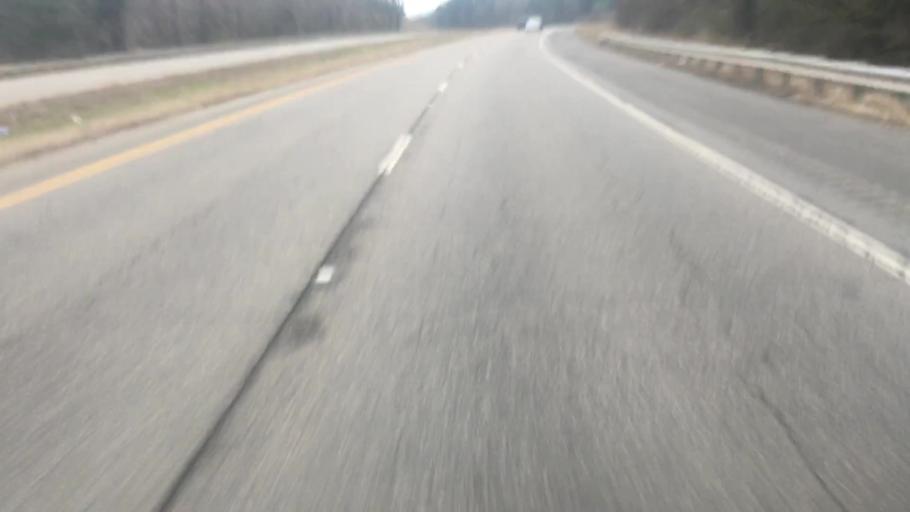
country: US
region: Alabama
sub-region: Walker County
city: Cordova
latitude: 33.8132
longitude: -87.1479
